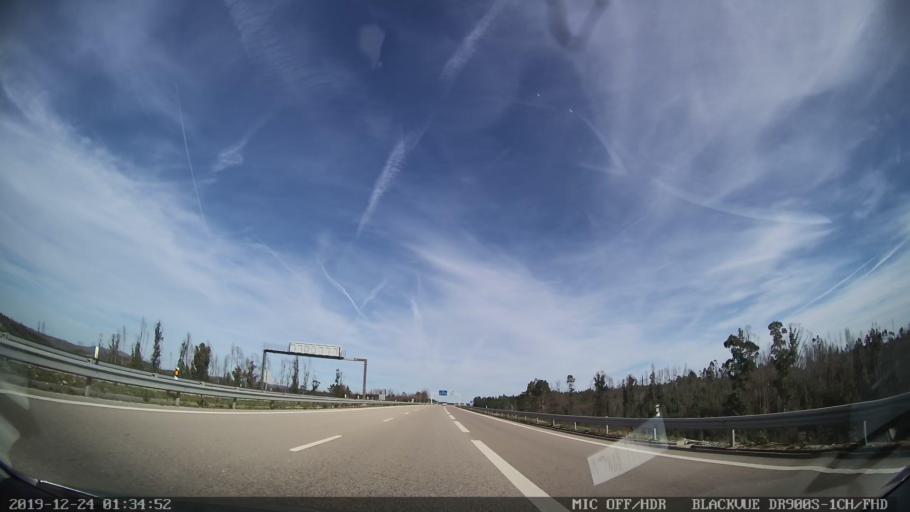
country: PT
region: Santarem
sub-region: Macao
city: Macao
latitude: 39.5084
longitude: -8.0199
